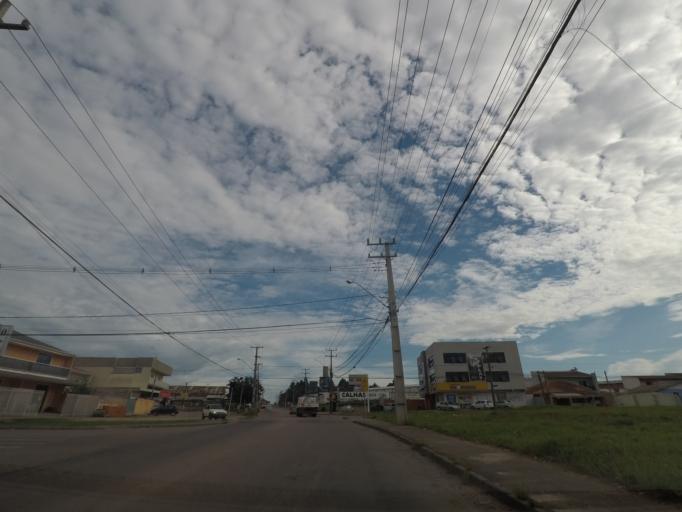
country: BR
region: Parana
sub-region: Araucaria
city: Araucaria
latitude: -25.6401
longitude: -49.3025
